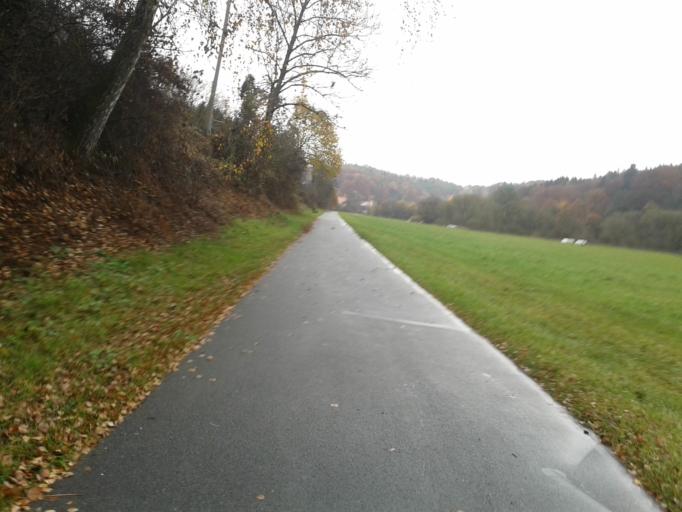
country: DE
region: Bavaria
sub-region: Regierungsbezirk Mittelfranken
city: Pommelsbrunn
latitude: 49.4986
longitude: 11.5385
